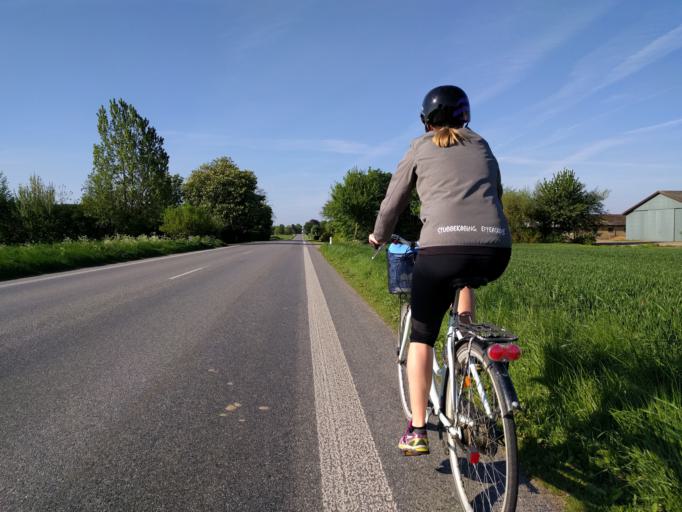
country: DK
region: Zealand
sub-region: Guldborgsund Kommune
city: Stubbekobing
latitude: 54.8712
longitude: 12.0245
